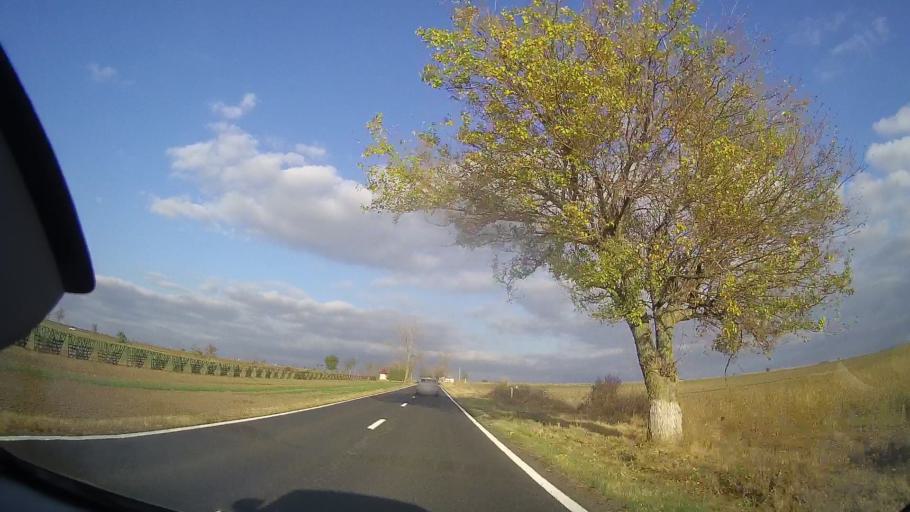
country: RO
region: Tulcea
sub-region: Comuna Topolog
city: Topolog
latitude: 44.8461
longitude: 28.3154
